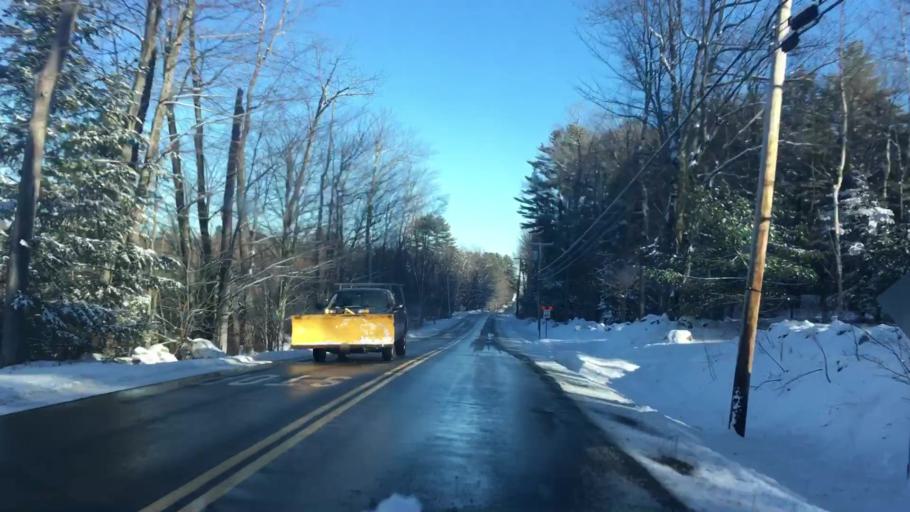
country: US
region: Maine
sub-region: Androscoggin County
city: Lisbon Falls
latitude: 43.9481
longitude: -70.1180
